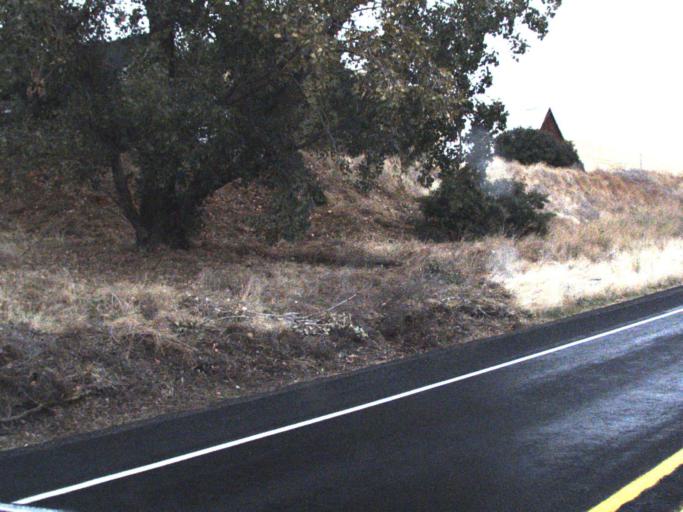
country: US
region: Washington
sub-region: Whitman County
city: Colfax
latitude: 46.8036
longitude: -117.5597
